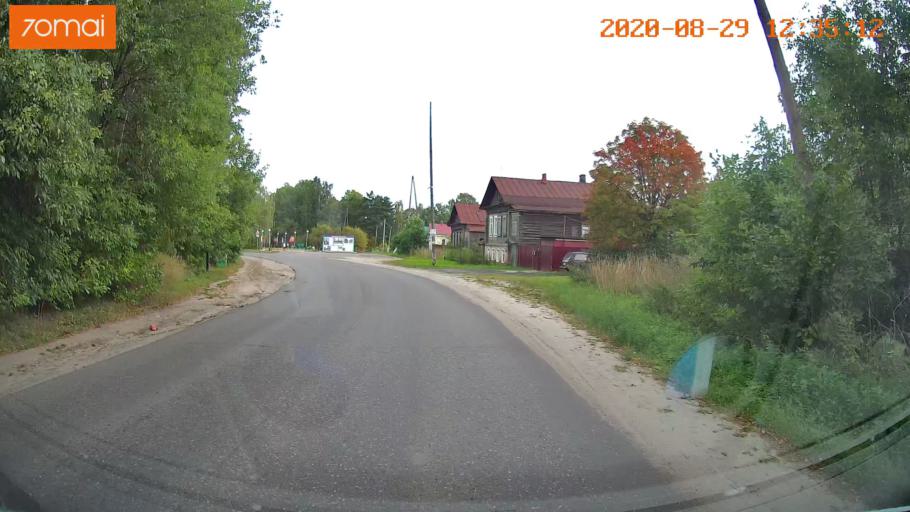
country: RU
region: Ivanovo
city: Yur'yevets
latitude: 57.3125
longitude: 43.1058
